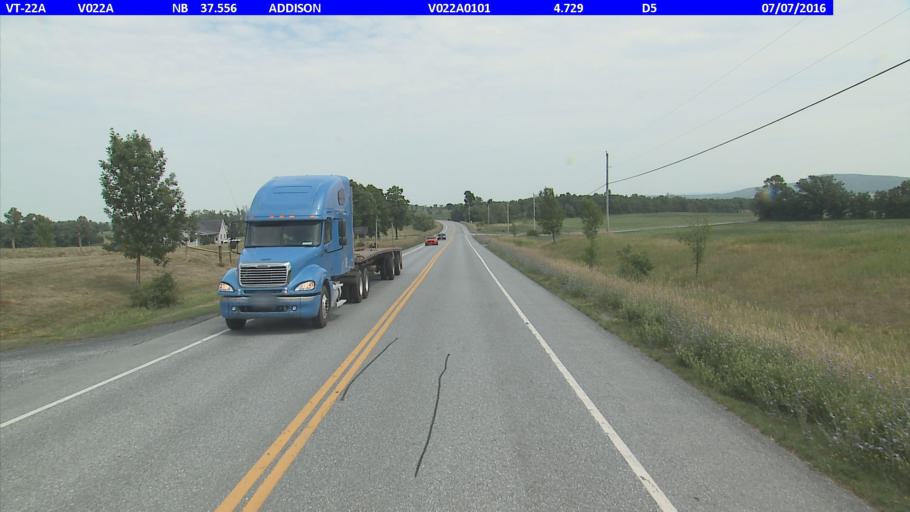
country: US
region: Vermont
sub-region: Addison County
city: Vergennes
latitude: 44.0974
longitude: -73.2995
